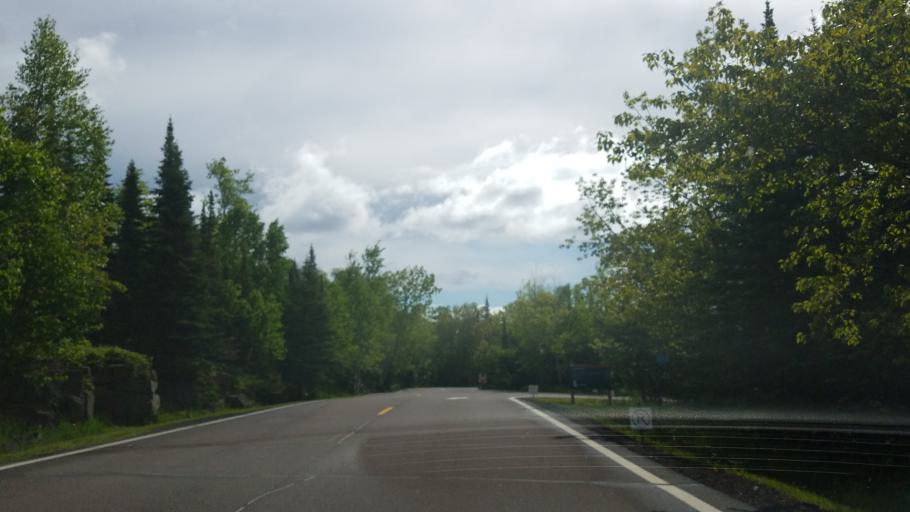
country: US
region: Minnesota
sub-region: Lake County
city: Silver Bay
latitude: 47.2021
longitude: -91.3688
